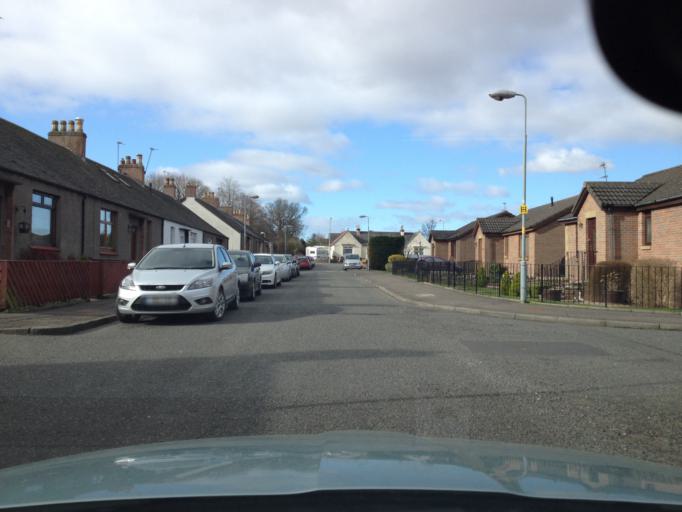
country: GB
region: Scotland
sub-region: West Lothian
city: Mid Calder
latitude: 55.9058
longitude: -3.4892
